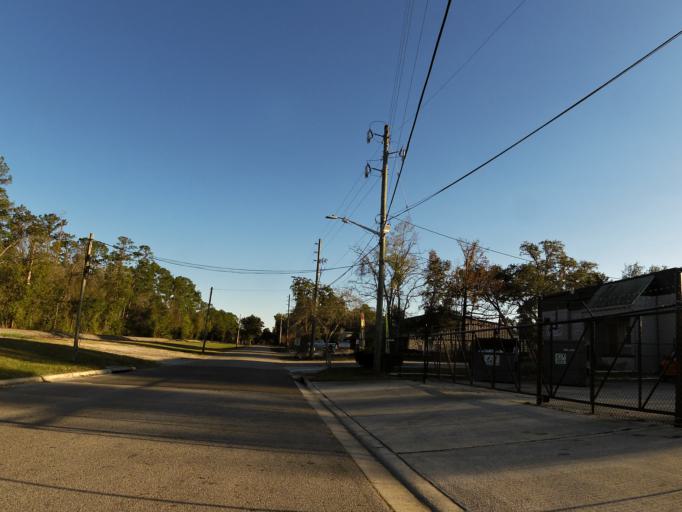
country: US
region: Florida
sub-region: Saint Johns County
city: Fruit Cove
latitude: 30.2057
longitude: -81.5789
